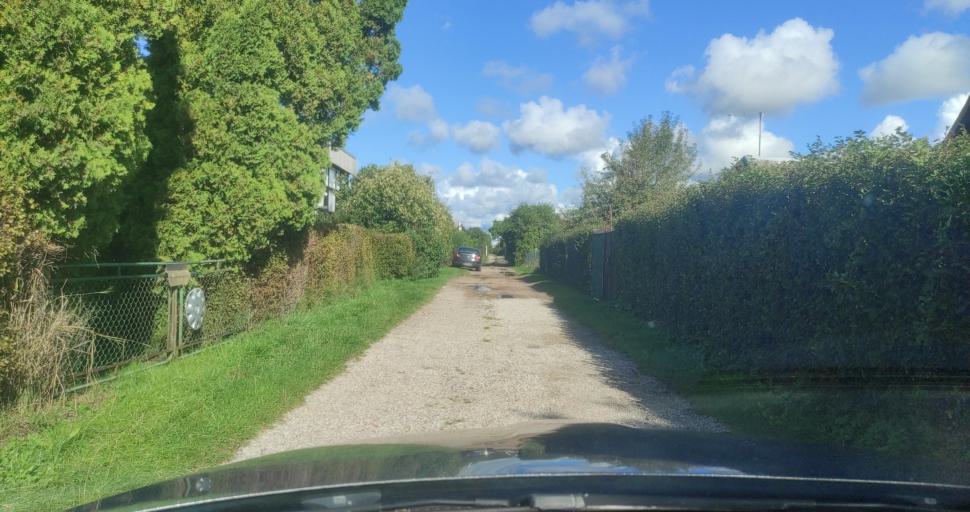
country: LV
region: Ventspils
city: Ventspils
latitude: 57.3677
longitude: 21.5995
